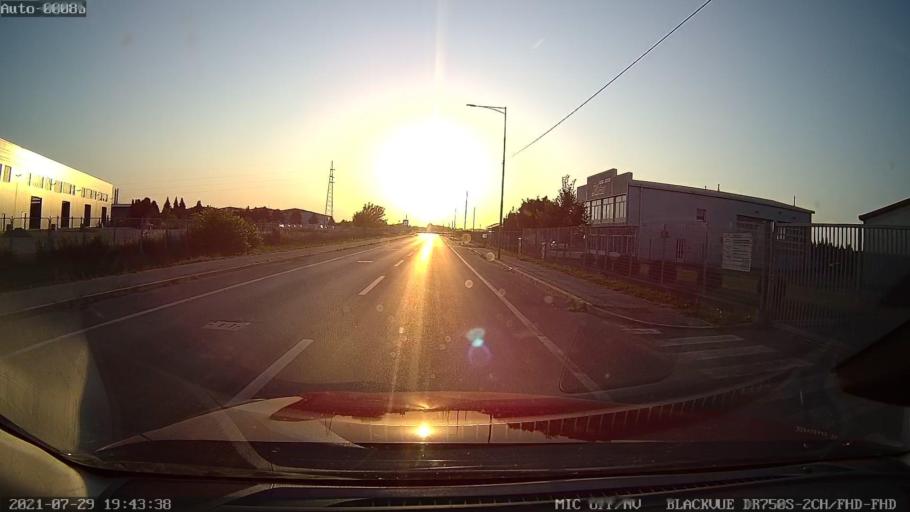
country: HR
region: Varazdinska
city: Ludbreg
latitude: 46.2567
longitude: 16.6019
